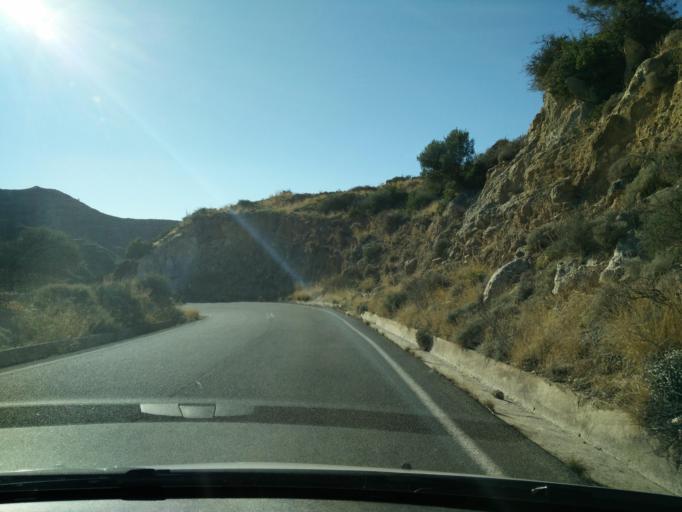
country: GR
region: Crete
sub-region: Nomos Lasithiou
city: Gra Liyia
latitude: 35.0153
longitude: 25.5771
